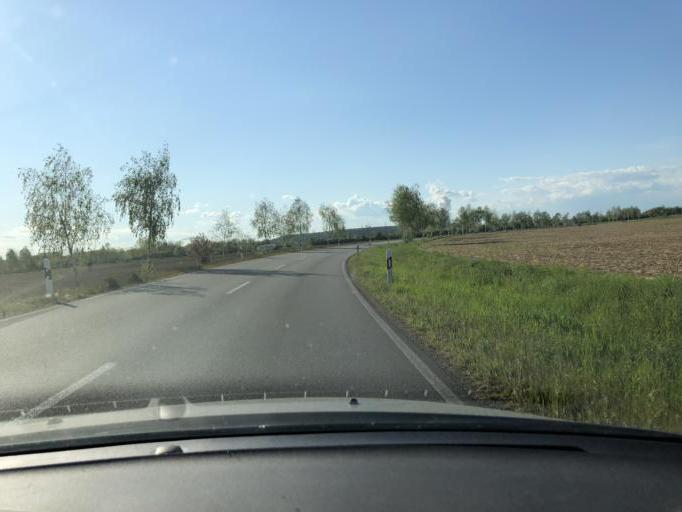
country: DE
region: Saxony
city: Neukieritzsch
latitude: 51.1541
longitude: 12.4248
